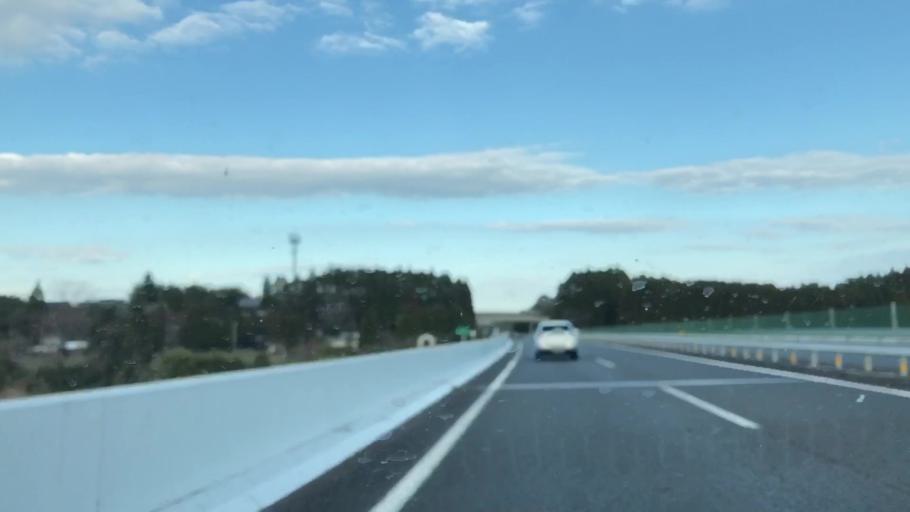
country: JP
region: Miyazaki
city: Miyazaki-shi
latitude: 31.8559
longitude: 131.3741
